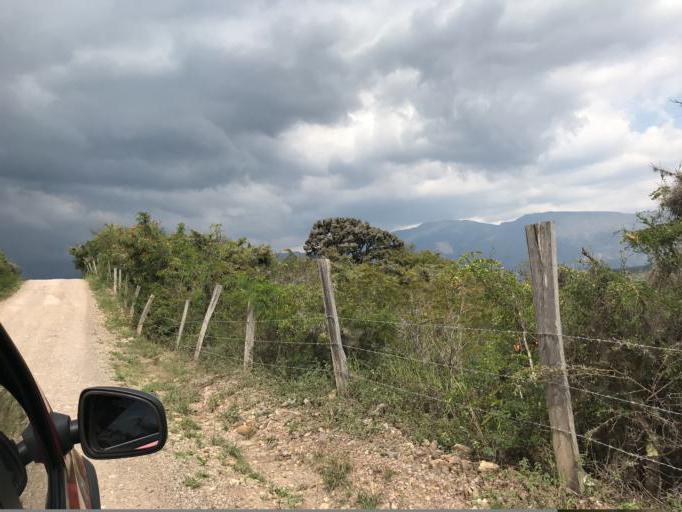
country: CO
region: Boyaca
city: Villa de Leiva
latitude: 5.6469
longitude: -73.5676
